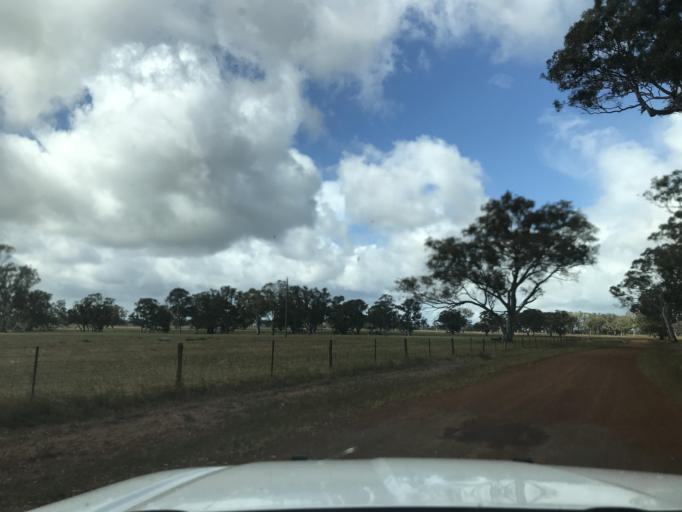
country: AU
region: South Australia
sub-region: Wattle Range
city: Penola
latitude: -37.2014
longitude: 141.3422
